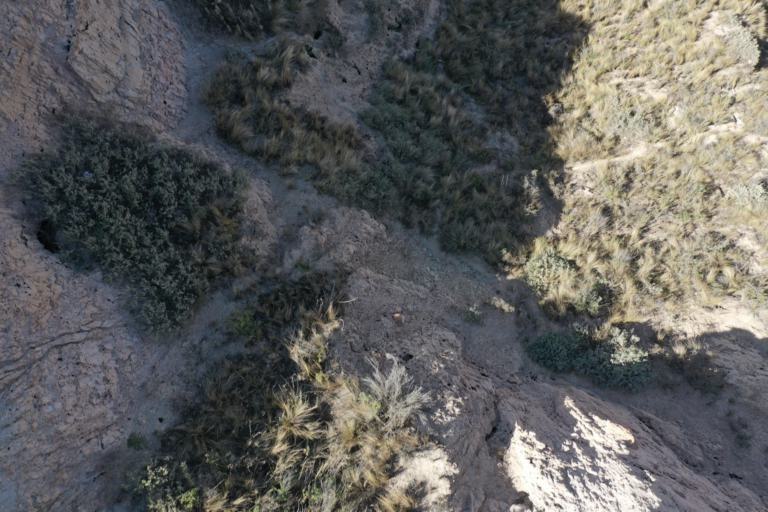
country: BO
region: La Paz
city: La Paz
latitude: -16.5509
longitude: -68.1292
